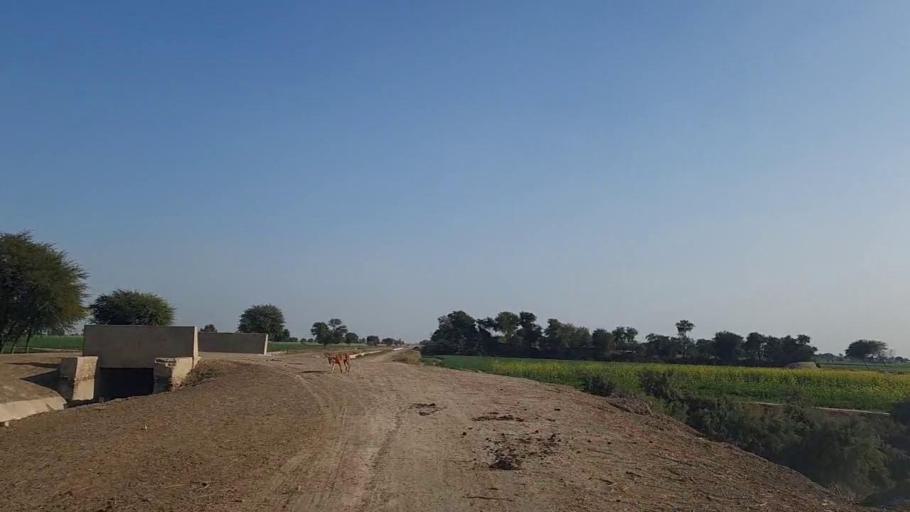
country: PK
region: Sindh
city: Shahpur Chakar
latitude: 26.1987
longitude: 68.6513
